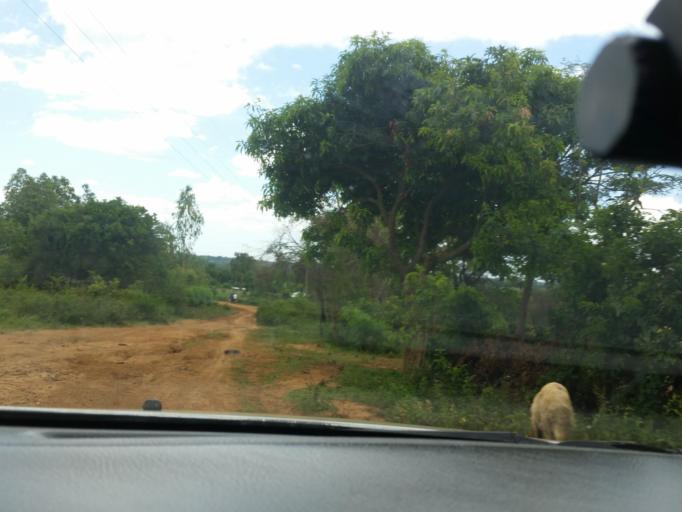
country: KE
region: Kakamega
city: Butere
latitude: 0.1118
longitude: 34.4076
